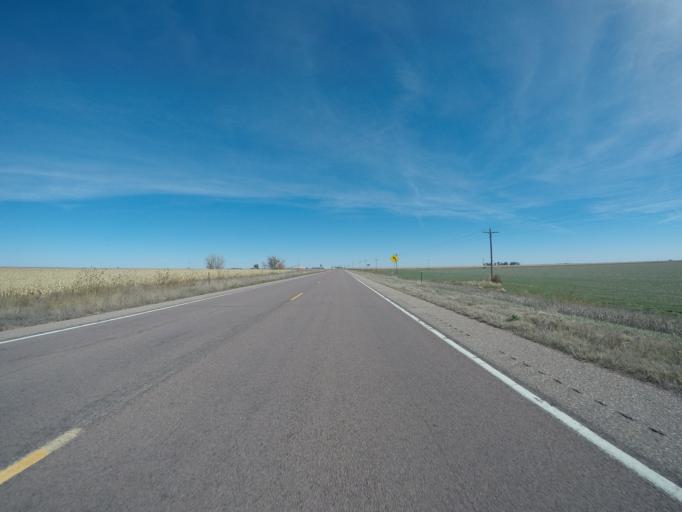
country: US
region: Colorado
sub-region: Kit Carson County
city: Burlington
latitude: 39.6572
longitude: -102.4433
